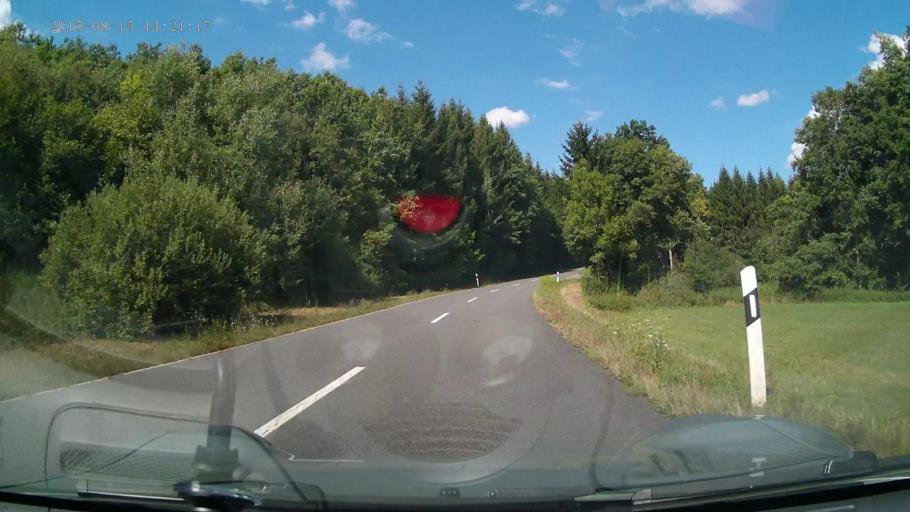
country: DE
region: Baden-Wuerttemberg
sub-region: Karlsruhe Region
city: Osterburken
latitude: 49.4458
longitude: 9.4026
